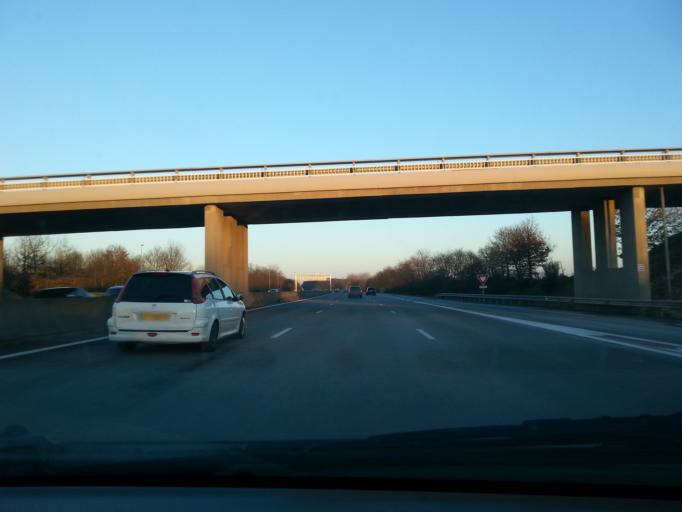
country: FR
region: Centre
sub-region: Departement d'Eure-et-Loir
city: Unverre
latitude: 48.2322
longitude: 1.0333
